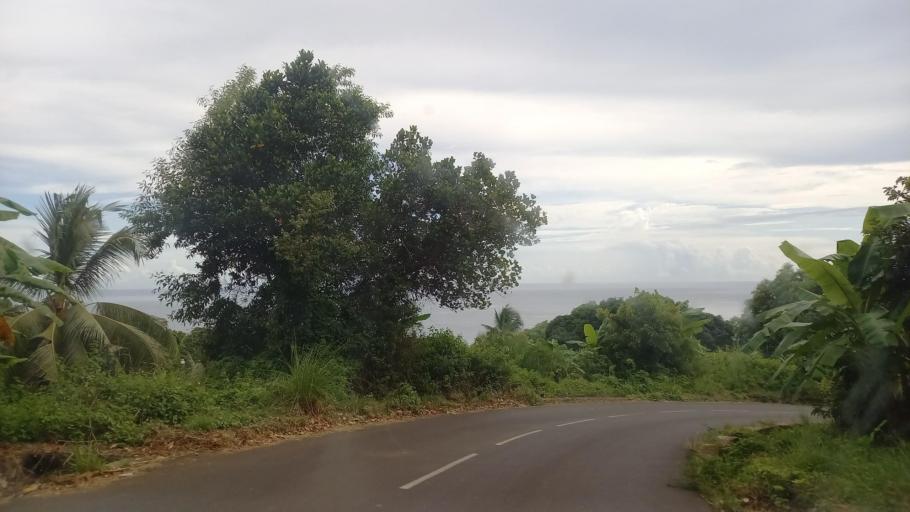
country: YT
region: Boueni
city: Boueni
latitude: -12.9051
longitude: 45.0849
